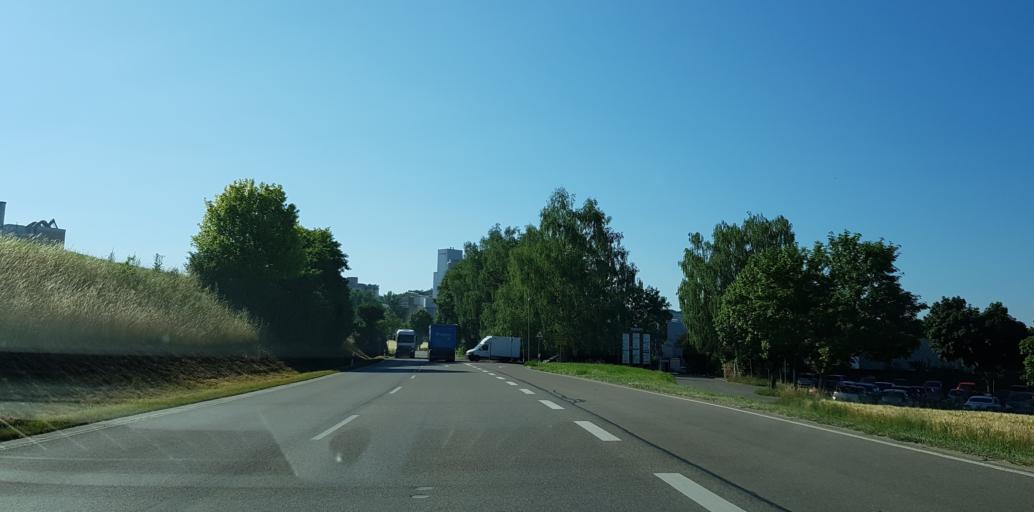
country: DE
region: Baden-Wuerttemberg
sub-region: Tuebingen Region
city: Allmendingen
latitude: 48.3363
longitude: 9.7242
